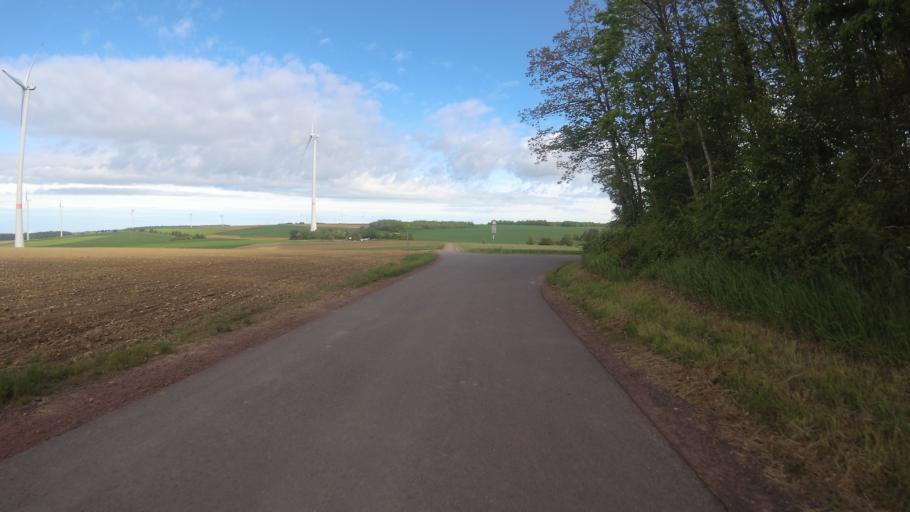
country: DE
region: Saarland
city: Orscholz
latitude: 49.4339
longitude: 6.5436
